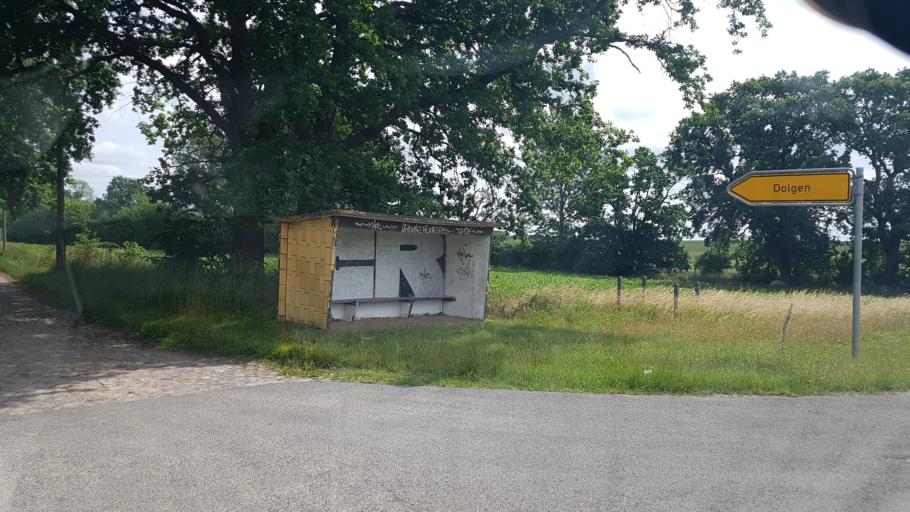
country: DE
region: Mecklenburg-Vorpommern
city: Strasburg
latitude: 53.4155
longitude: 13.7184
